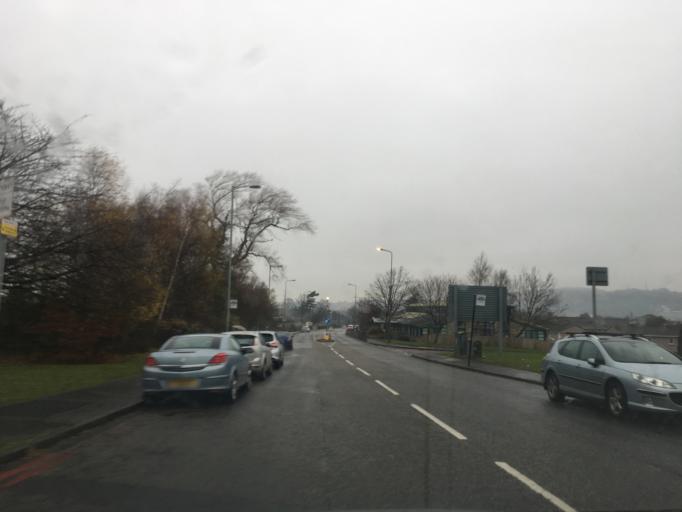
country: GB
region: Scotland
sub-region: Edinburgh
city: Colinton
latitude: 55.9270
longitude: -3.2708
